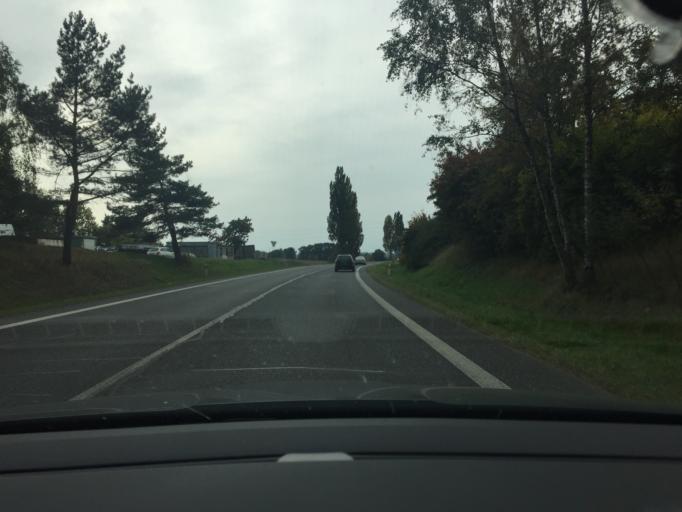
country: CZ
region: Central Bohemia
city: Milin
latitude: 49.6566
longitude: 14.0600
